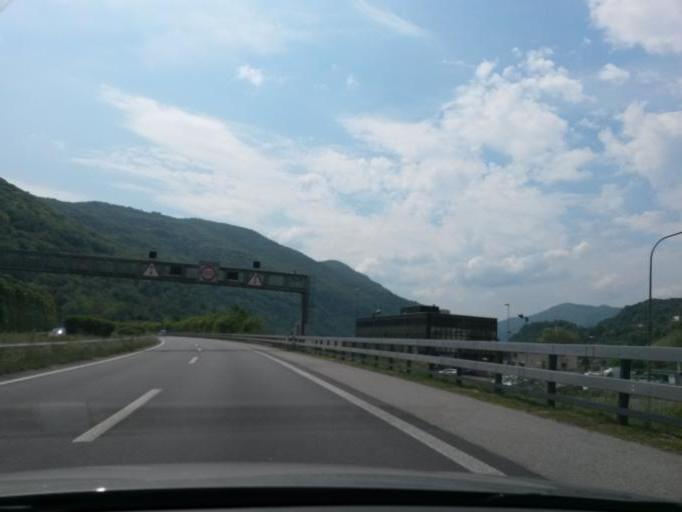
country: CH
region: Ticino
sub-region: Lugano District
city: Montagnola
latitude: 45.9687
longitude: 8.9256
